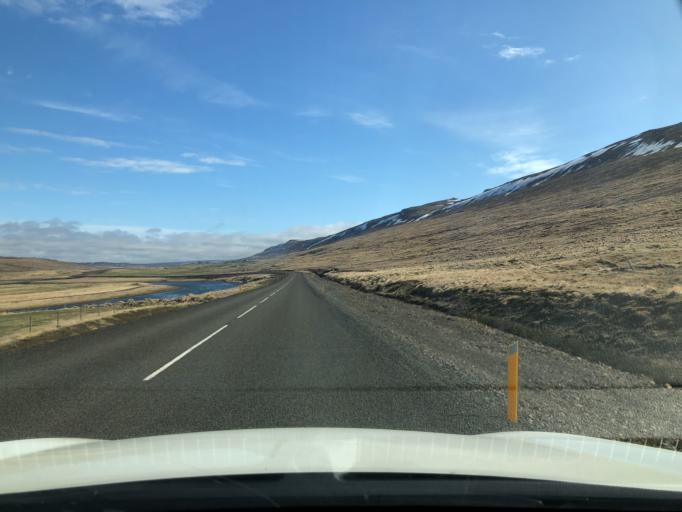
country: IS
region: West
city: Borgarnes
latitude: 65.1375
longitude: -21.6017
